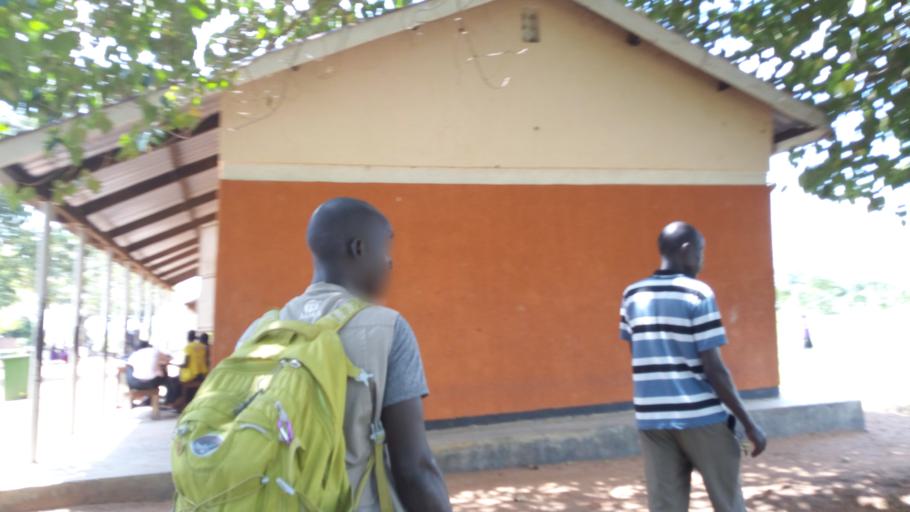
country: UG
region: Northern Region
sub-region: Adjumani District
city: Adjumani
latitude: 3.3020
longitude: 31.8583
